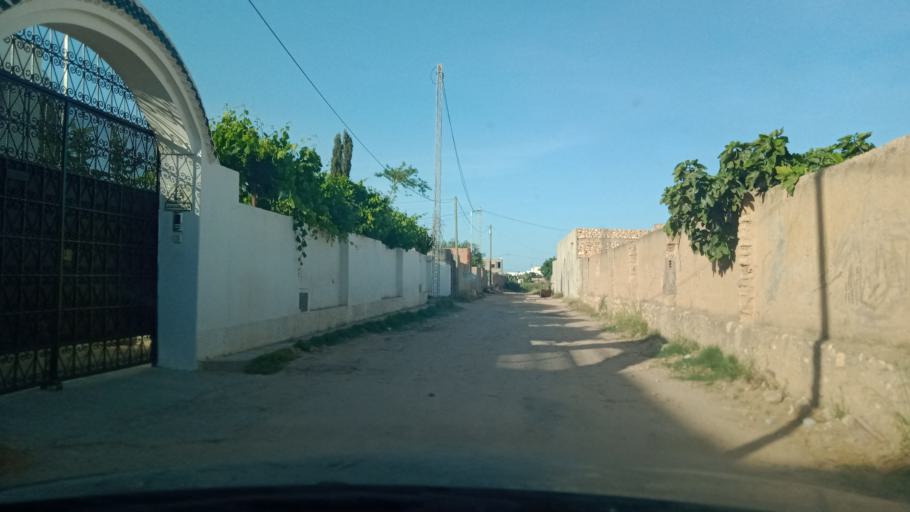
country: TN
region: Safaqis
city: Sfax
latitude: 34.8175
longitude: 10.7386
